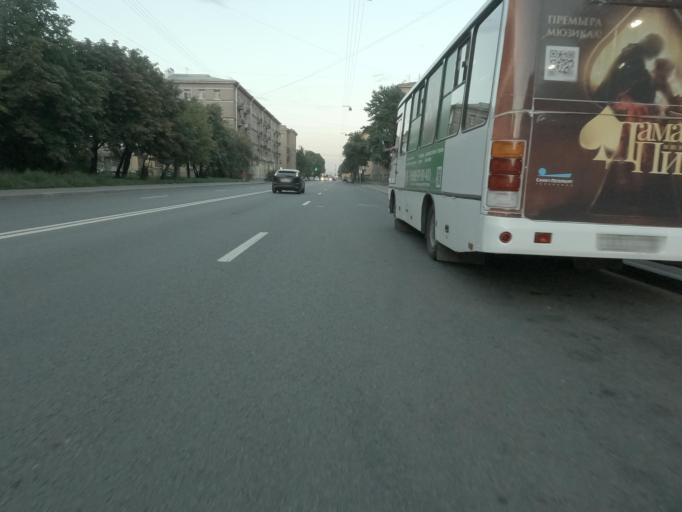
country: RU
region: St.-Petersburg
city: Vasyl'evsky Ostrov
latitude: 59.9092
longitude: 30.2438
